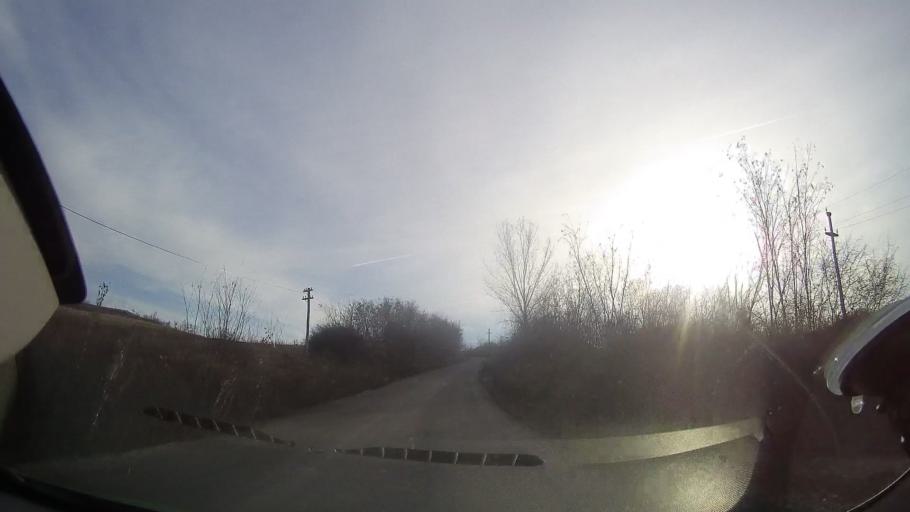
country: RO
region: Bihor
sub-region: Comuna Sarbi
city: Burzuc
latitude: 47.1672
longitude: 22.1604
